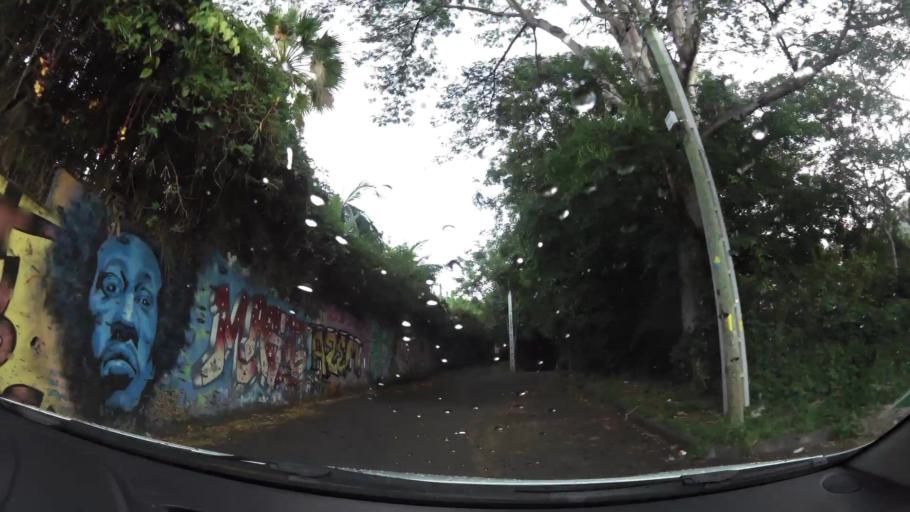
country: RE
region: Reunion
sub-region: Reunion
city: Saint-Denis
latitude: -20.9022
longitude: 55.4420
